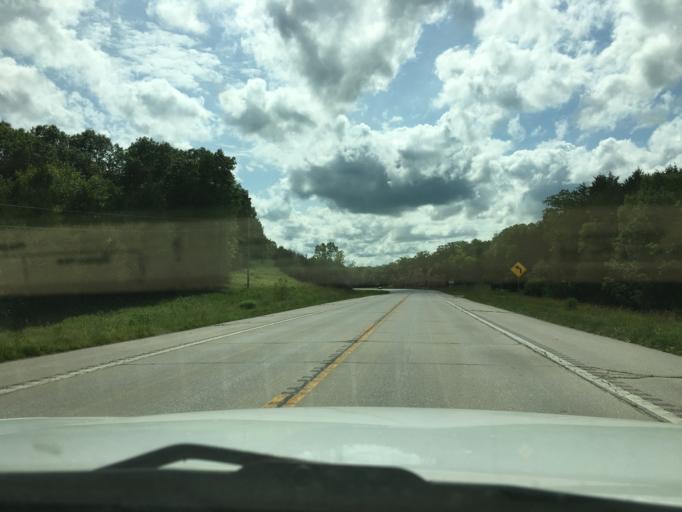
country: US
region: Missouri
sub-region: Franklin County
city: Gerald
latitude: 38.4234
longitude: -91.2758
